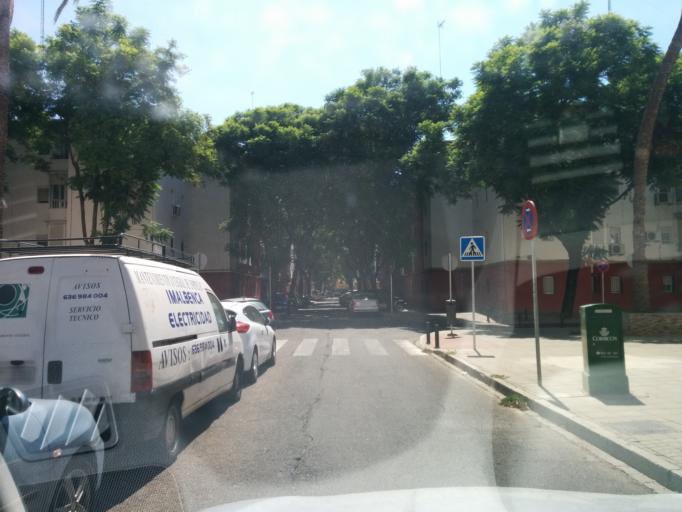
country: ES
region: Andalusia
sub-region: Provincia de Sevilla
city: San Juan de Aznalfarache
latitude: 37.3761
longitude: -6.0131
